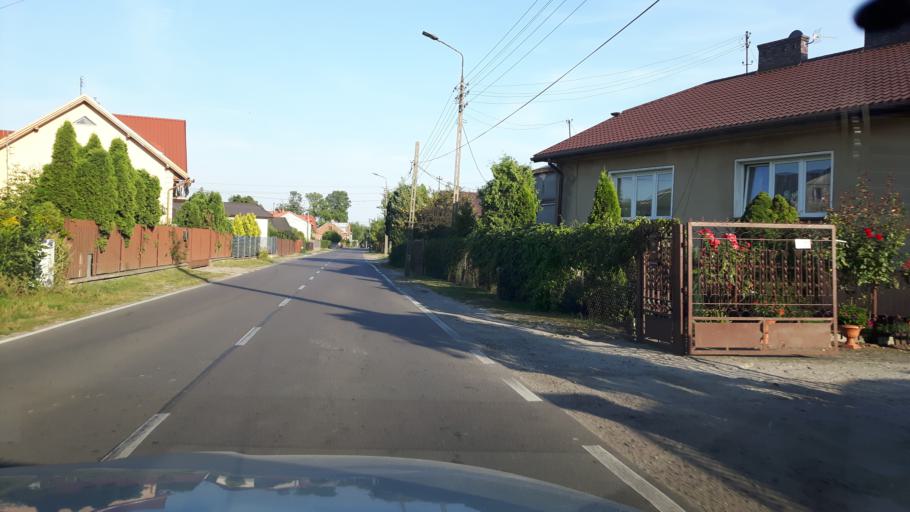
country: PL
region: Masovian Voivodeship
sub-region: Powiat wolominski
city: Slupno
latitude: 52.3626
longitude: 21.1637
